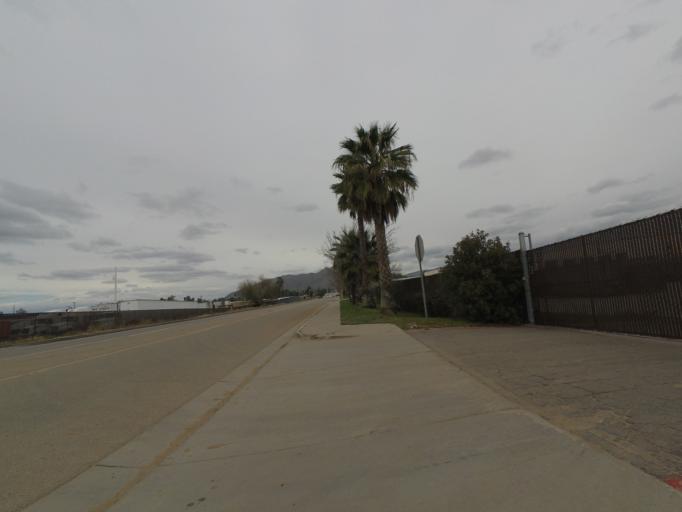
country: US
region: California
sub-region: Riverside County
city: March Air Force Base
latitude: 33.9145
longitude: -117.2787
